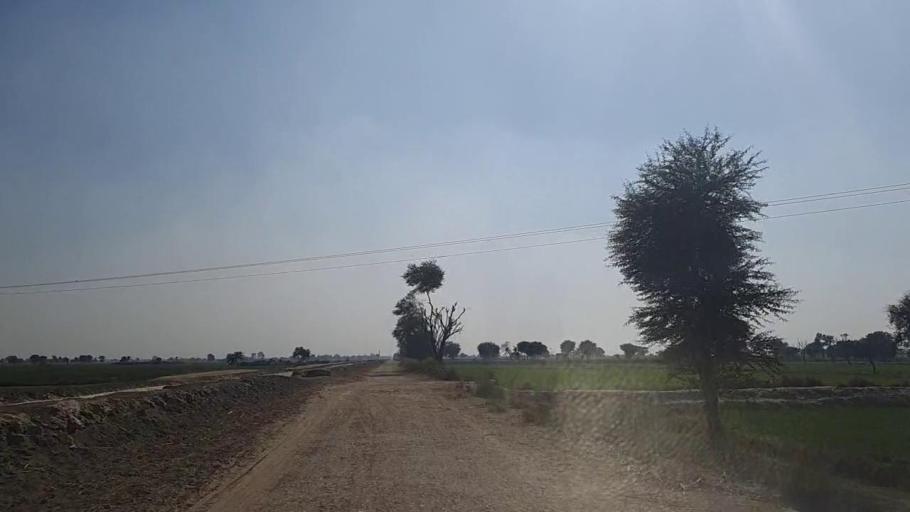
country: PK
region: Sindh
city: Shahpur Chakar
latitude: 26.2053
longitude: 68.5838
